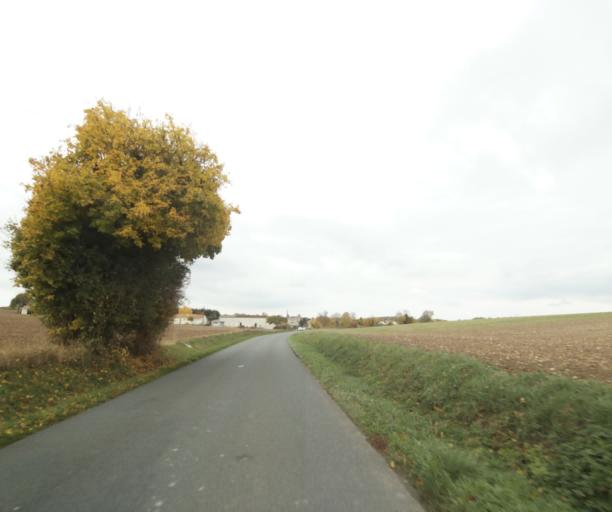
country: FR
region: Poitou-Charentes
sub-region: Departement de la Charente-Maritime
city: Bussac-sur-Charente
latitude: 45.7775
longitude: -0.6727
